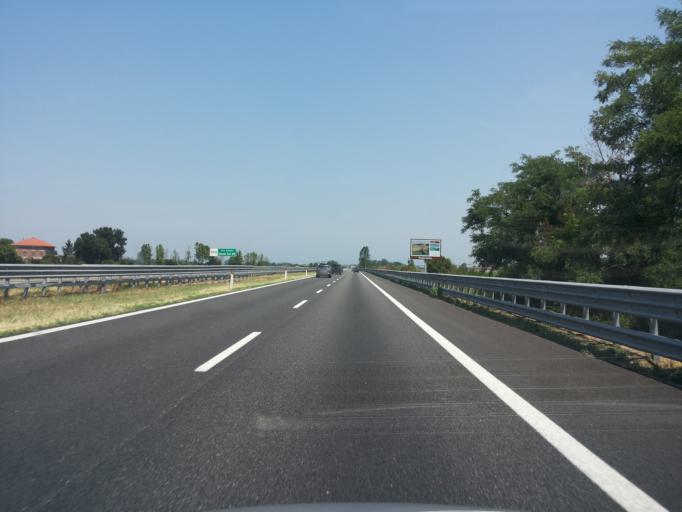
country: IT
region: Lombardy
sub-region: Provincia di Cremona
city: Corte de' Frati
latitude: 45.2278
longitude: 10.1153
